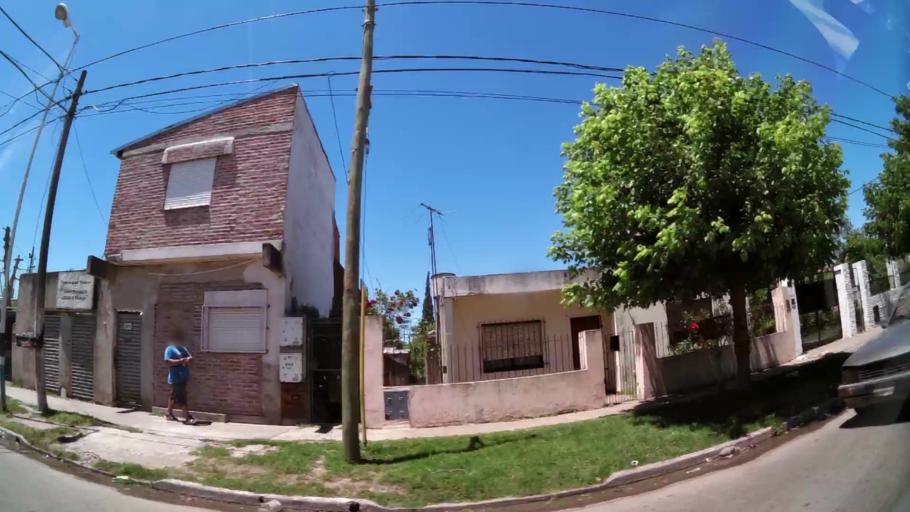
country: AR
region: Buenos Aires
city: Hurlingham
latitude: -34.5099
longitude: -58.7110
